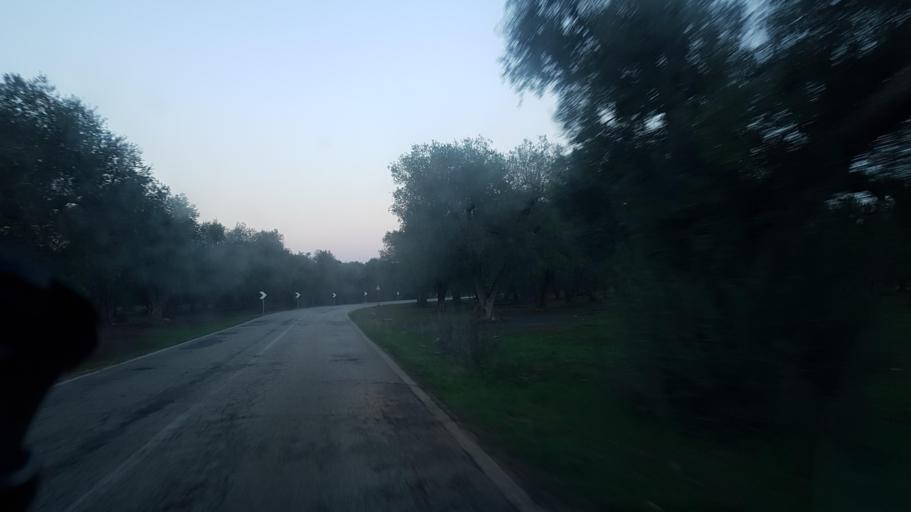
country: IT
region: Apulia
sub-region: Provincia di Brindisi
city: Latiano
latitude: 40.5709
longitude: 17.6902
